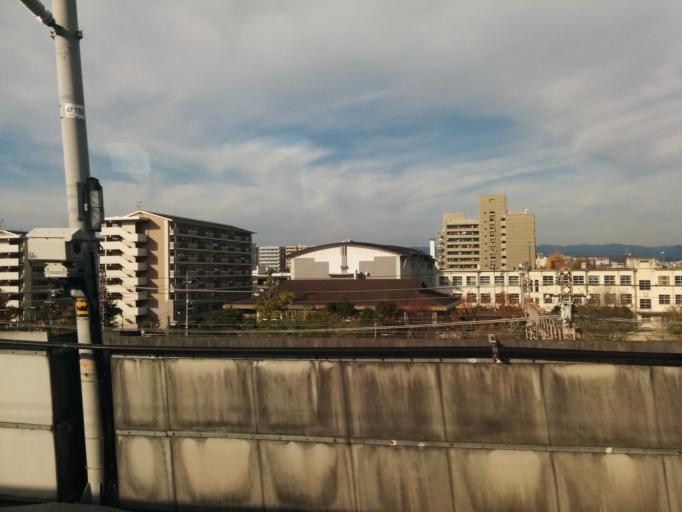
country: JP
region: Kyoto
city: Kyoto
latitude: 34.9853
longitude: 135.7667
